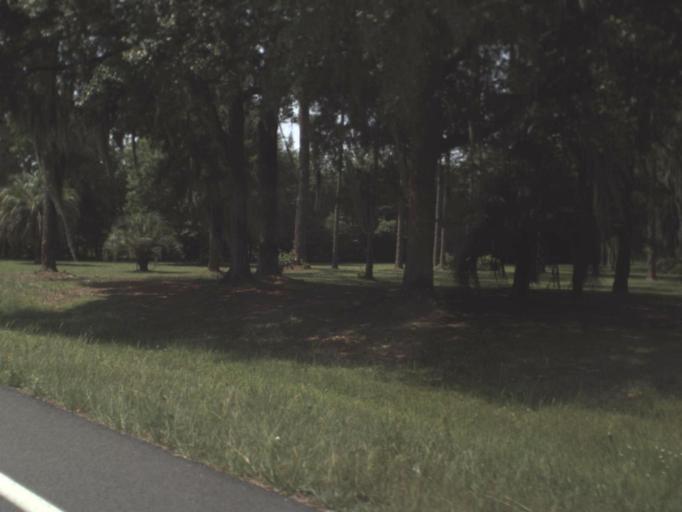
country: US
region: Florida
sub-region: Hamilton County
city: Jasper
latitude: 30.5292
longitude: -82.9680
